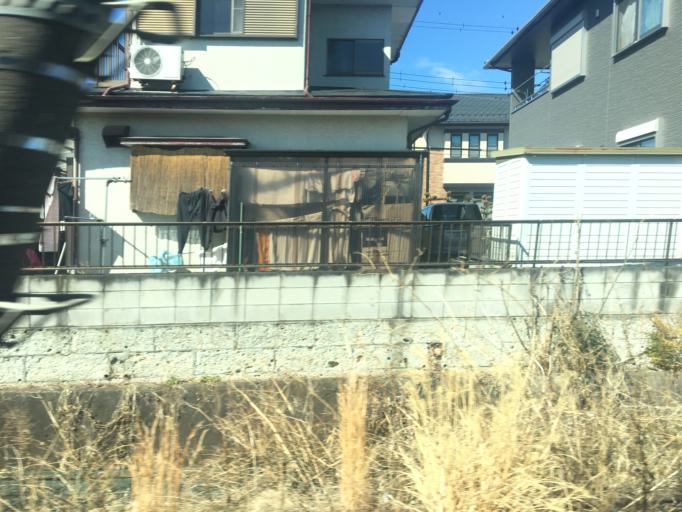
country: JP
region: Tochigi
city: Utsunomiya-shi
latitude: 36.4959
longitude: 139.8772
